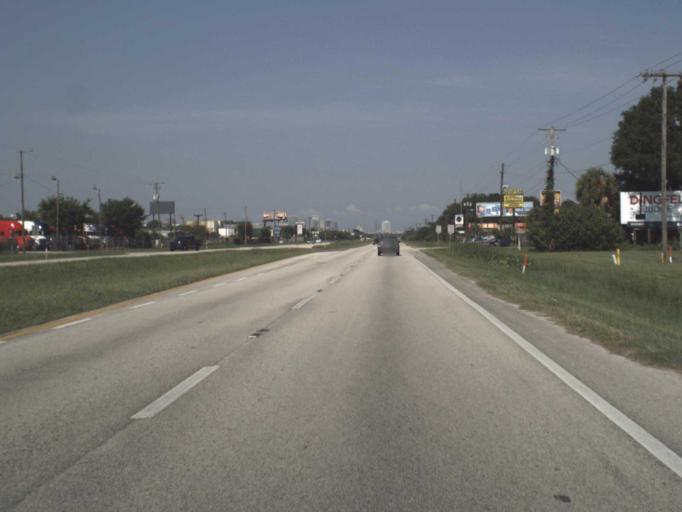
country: US
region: Florida
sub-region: Hillsborough County
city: Palm River-Clair Mel
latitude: 27.9523
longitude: -82.3867
